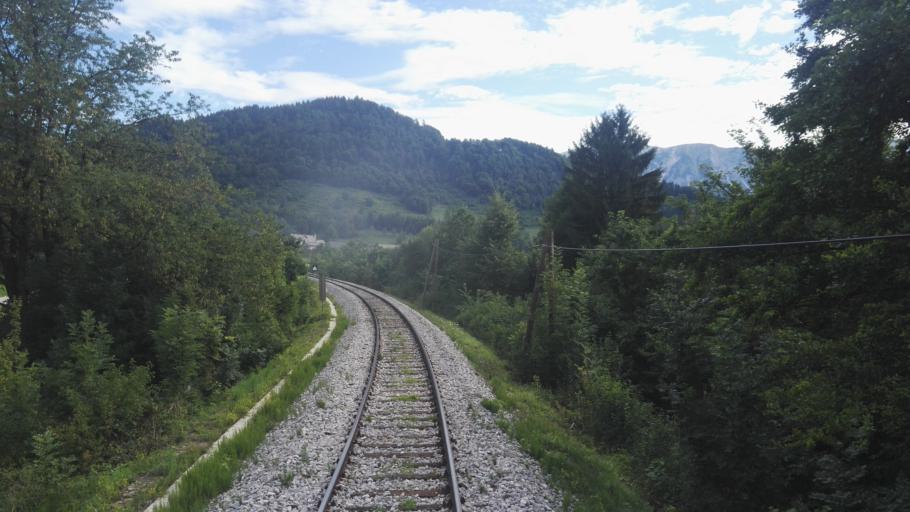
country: SI
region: Gorje
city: Zgornje Gorje
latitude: 46.3821
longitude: 14.0904
